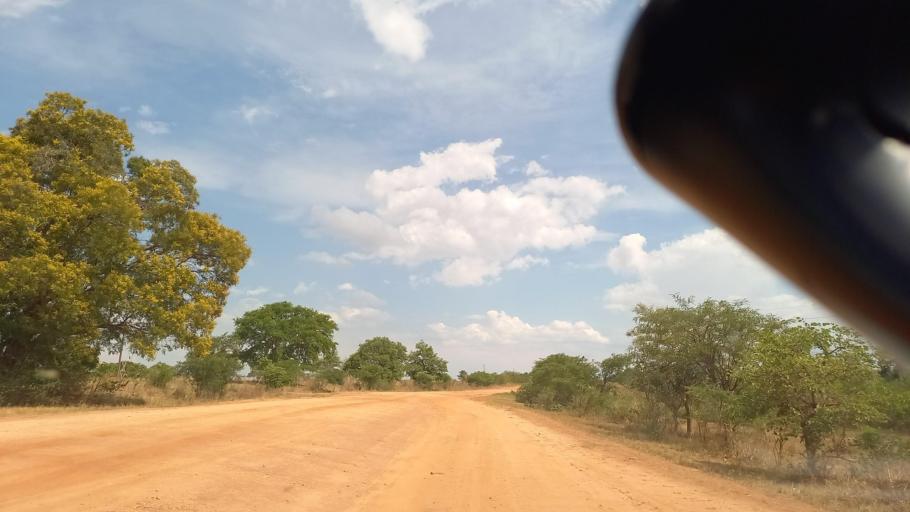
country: ZM
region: Lusaka
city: Kafue
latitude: -16.1220
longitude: 28.0408
